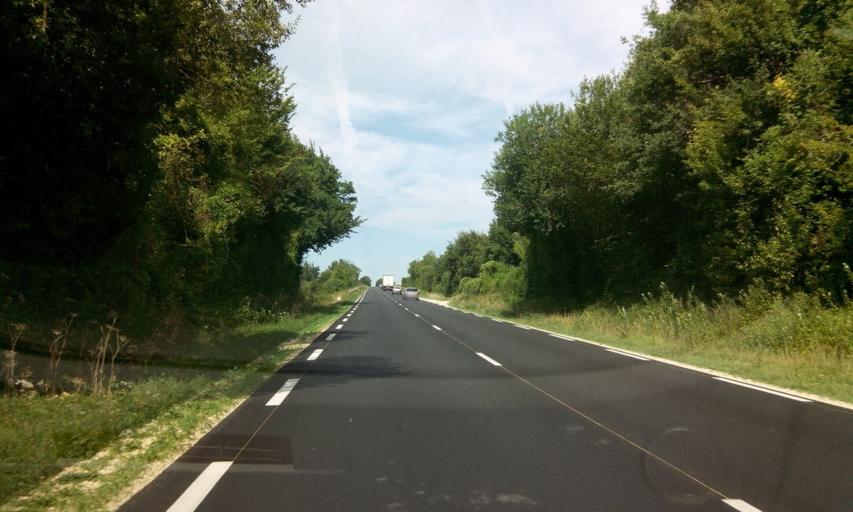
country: FR
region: Poitou-Charentes
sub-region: Departement des Deux-Sevres
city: Sauze-Vaussais
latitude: 46.1404
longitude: 0.0928
